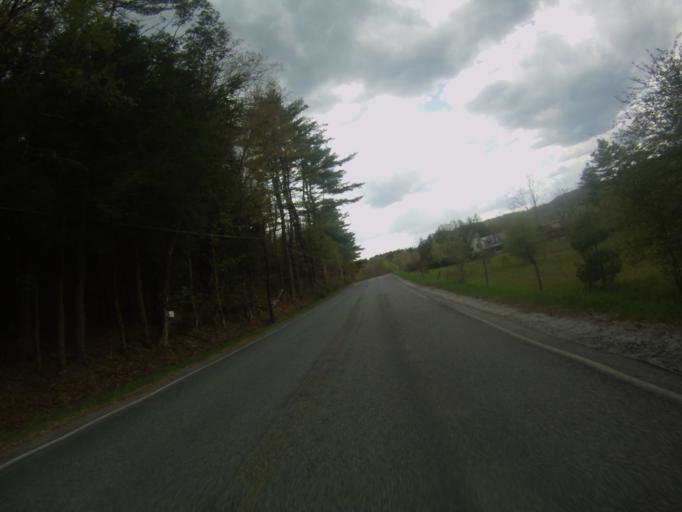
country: US
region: New York
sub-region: Essex County
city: Mineville
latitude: 44.0528
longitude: -73.5400
